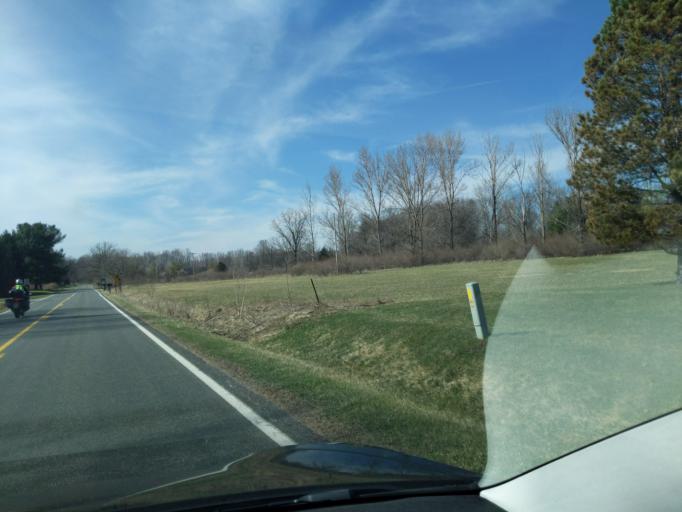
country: US
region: Michigan
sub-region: Ingham County
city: Stockbridge
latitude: 42.4809
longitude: -84.2115
